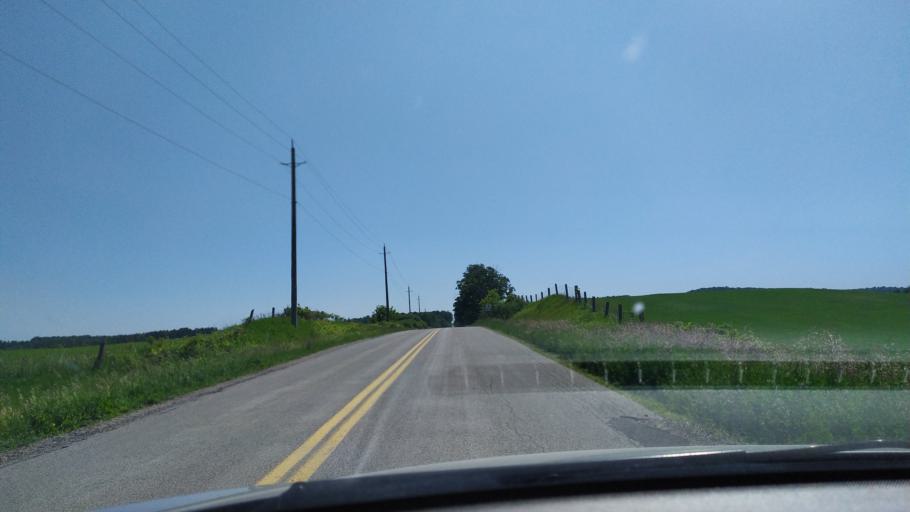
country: CA
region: Ontario
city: Waterloo
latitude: 43.4705
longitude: -80.6408
